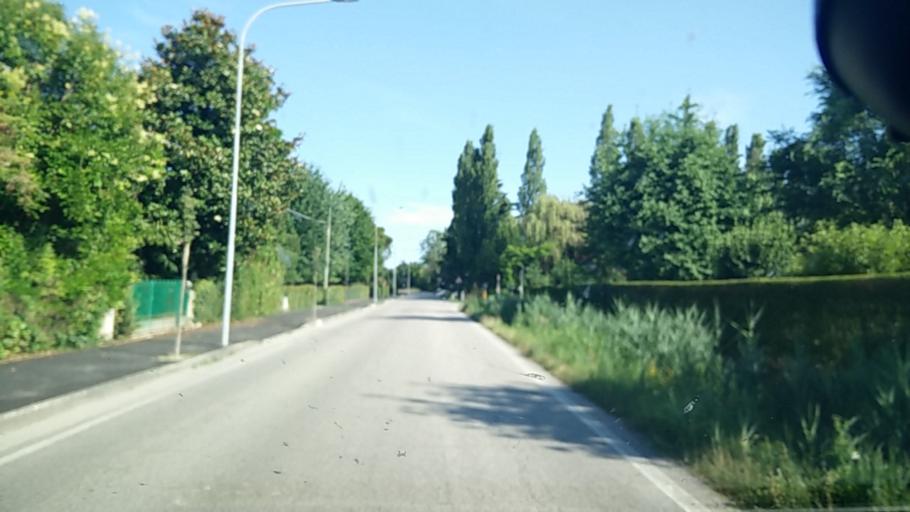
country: IT
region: Veneto
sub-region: Provincia di Treviso
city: San Biagio di Callalta
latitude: 45.6805
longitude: 12.4001
